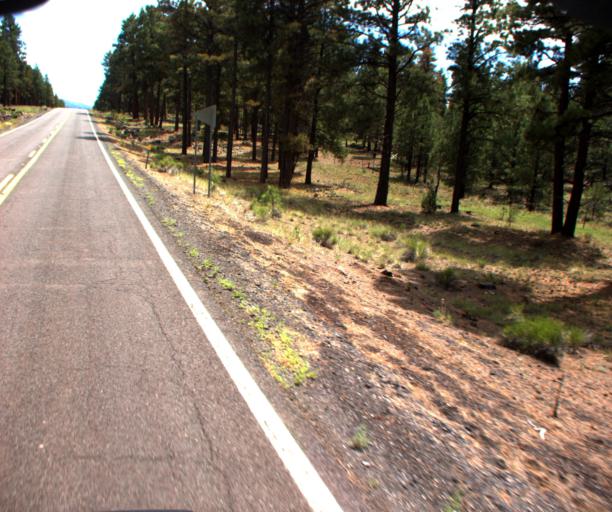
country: US
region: Arizona
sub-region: Coconino County
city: Parks
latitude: 35.4572
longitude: -111.7765
